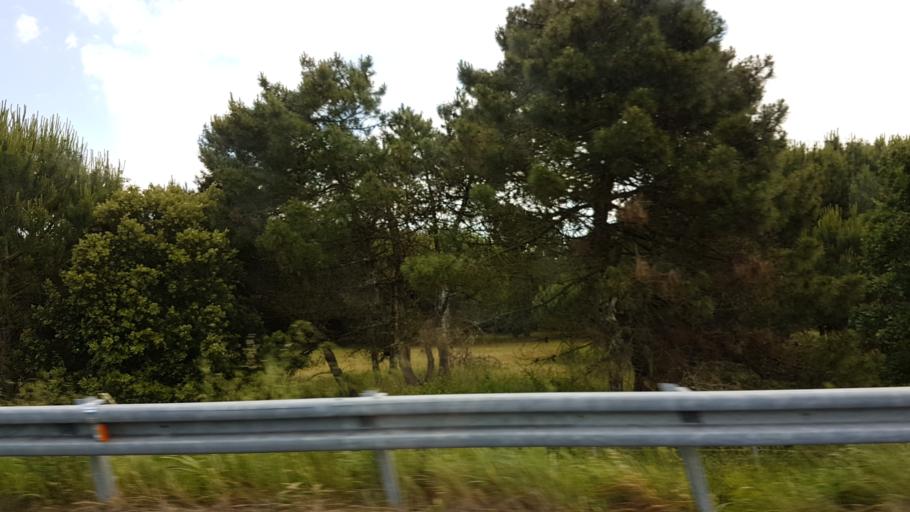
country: IT
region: Tuscany
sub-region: Provincia di Livorno
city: Guasticce
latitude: 43.6276
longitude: 10.3570
